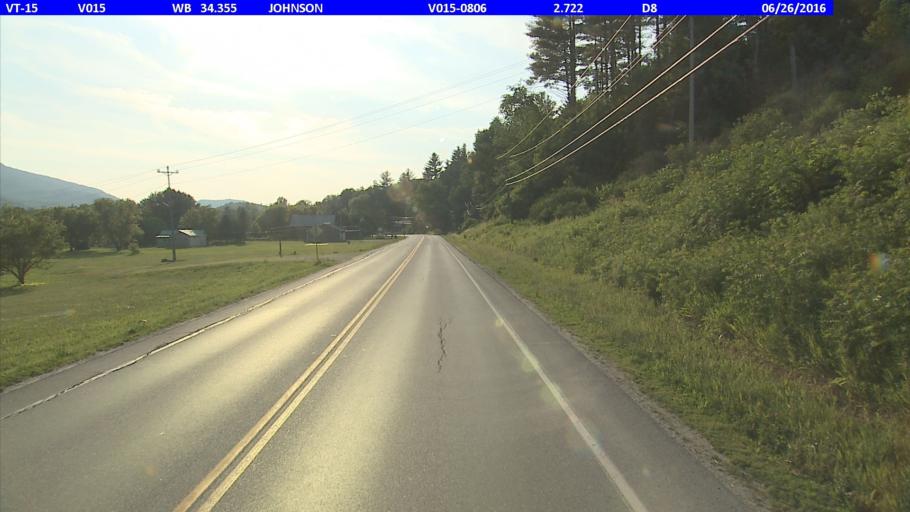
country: US
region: Vermont
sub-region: Lamoille County
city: Johnson
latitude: 44.6418
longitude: -72.7027
